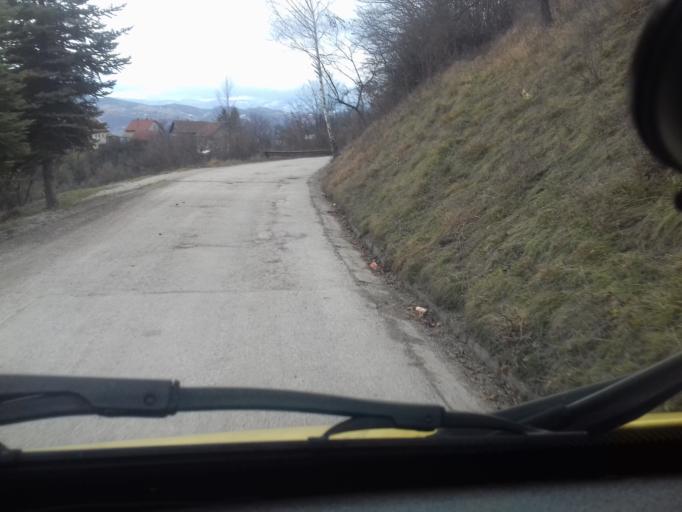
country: BA
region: Federation of Bosnia and Herzegovina
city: Zenica
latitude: 44.2200
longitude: 17.9364
